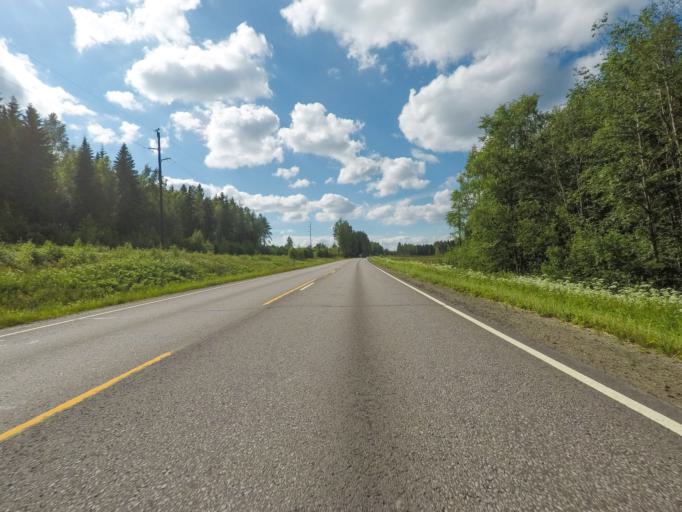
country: FI
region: Southern Savonia
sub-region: Savonlinna
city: Kerimaeki
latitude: 61.8437
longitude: 29.1955
